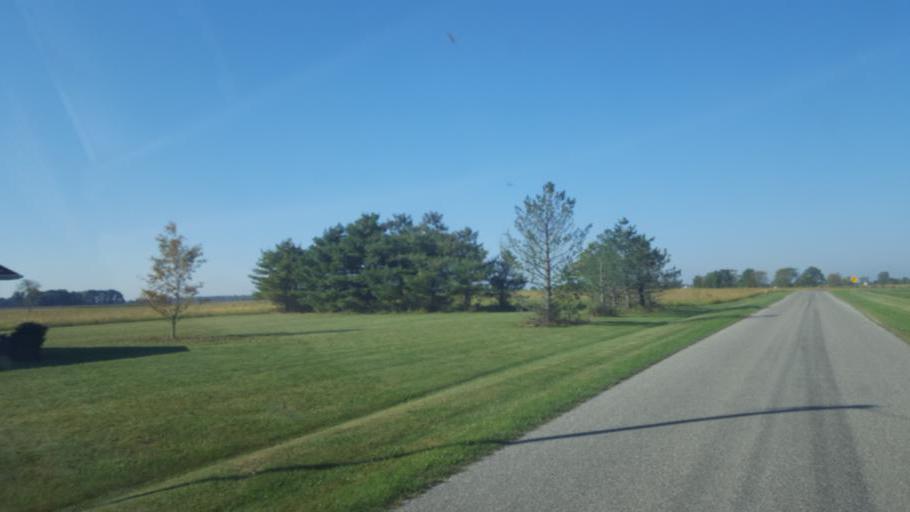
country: US
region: Ohio
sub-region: Union County
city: Richwood
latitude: 40.4945
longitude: -83.4669
